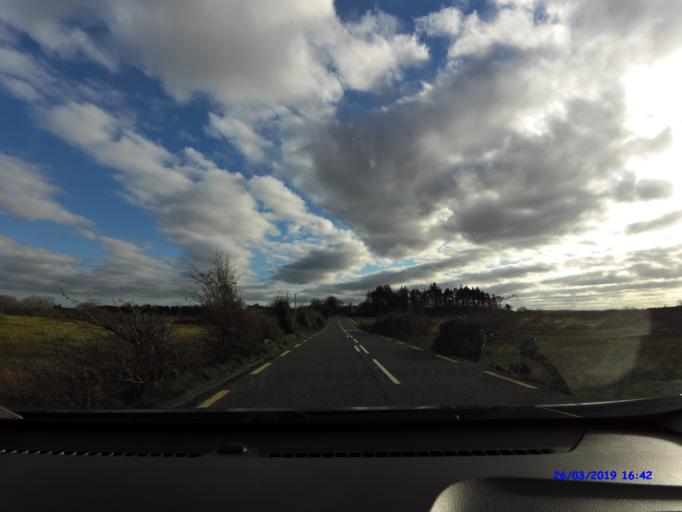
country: IE
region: Connaught
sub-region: Maigh Eo
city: Ballyhaunis
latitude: 53.8638
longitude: -8.7637
